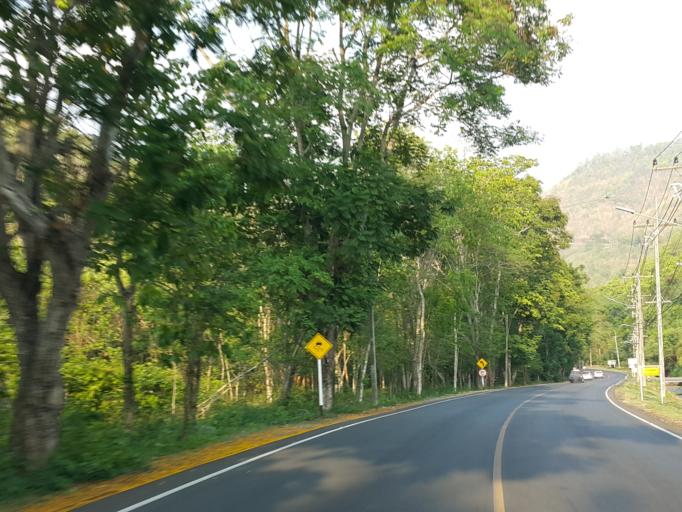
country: TH
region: Kanchanaburi
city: Si Sawat
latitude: 14.3847
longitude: 99.1372
